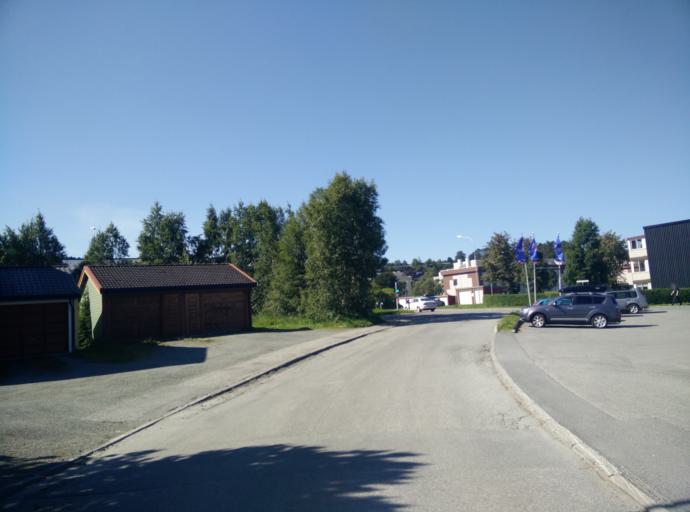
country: NO
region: Sor-Trondelag
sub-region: Trondheim
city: Trondheim
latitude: 63.4087
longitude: 10.3614
